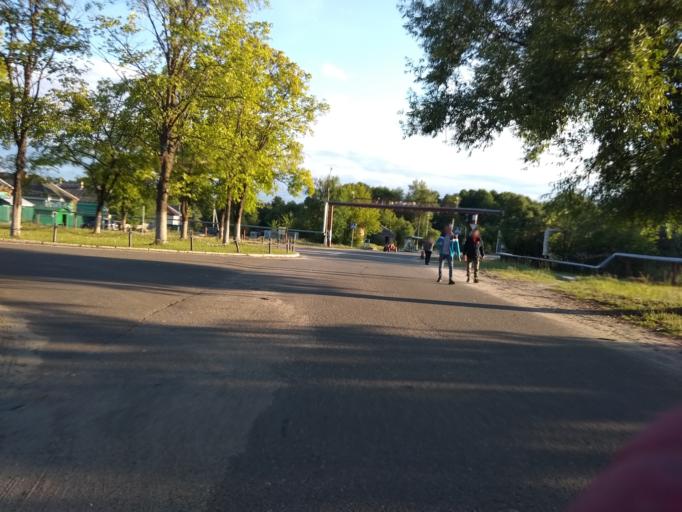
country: RU
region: Moskovskaya
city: Misheronskiy
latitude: 55.7179
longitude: 39.7414
